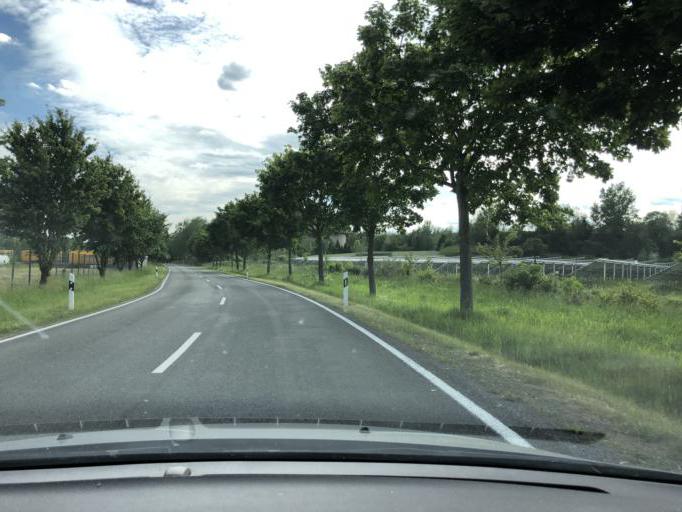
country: DE
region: Saxony
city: Trebsen
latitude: 51.2860
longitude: 12.7379
